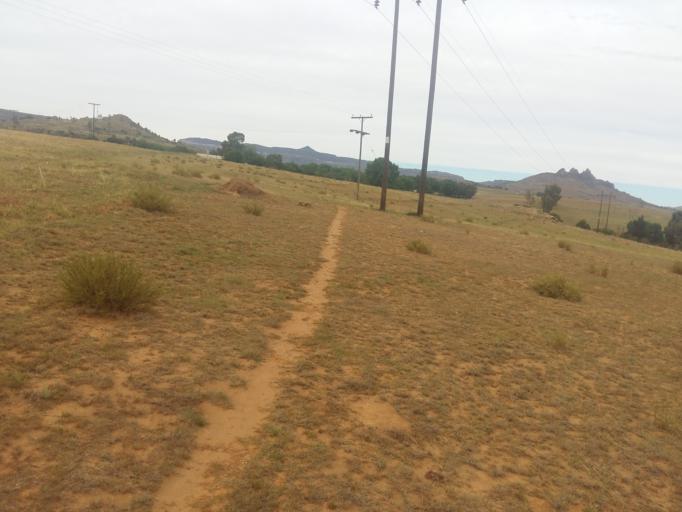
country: LS
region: Mafeteng
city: Mafeteng
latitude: -29.6936
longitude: 27.4301
